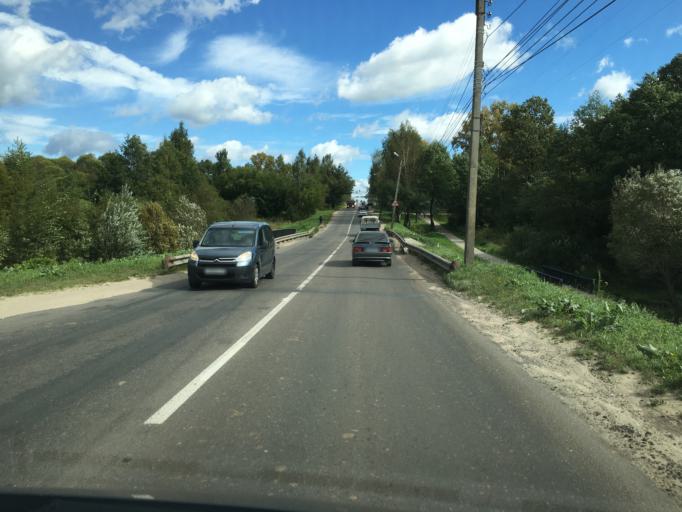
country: RU
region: Kaluga
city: Kaluga
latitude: 54.5442
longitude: 36.3252
